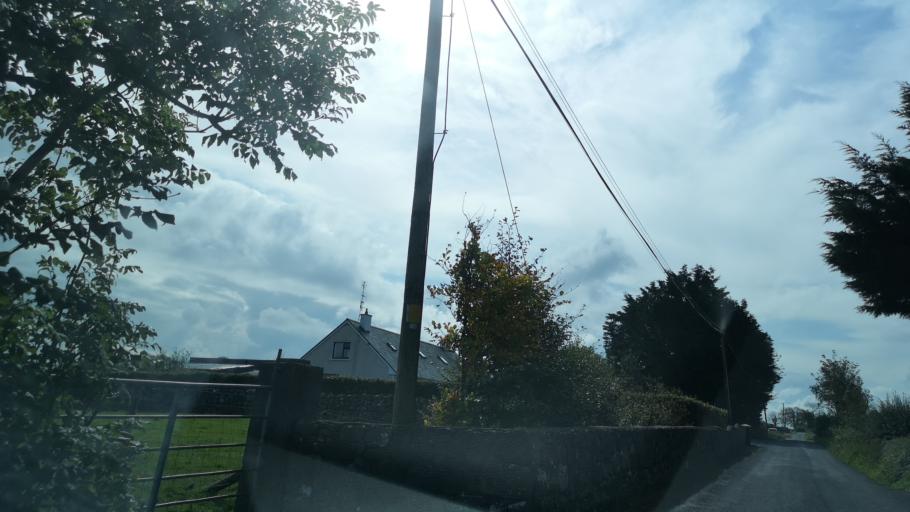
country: IE
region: Connaught
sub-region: County Galway
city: Athenry
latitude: 53.3078
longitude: -8.8096
